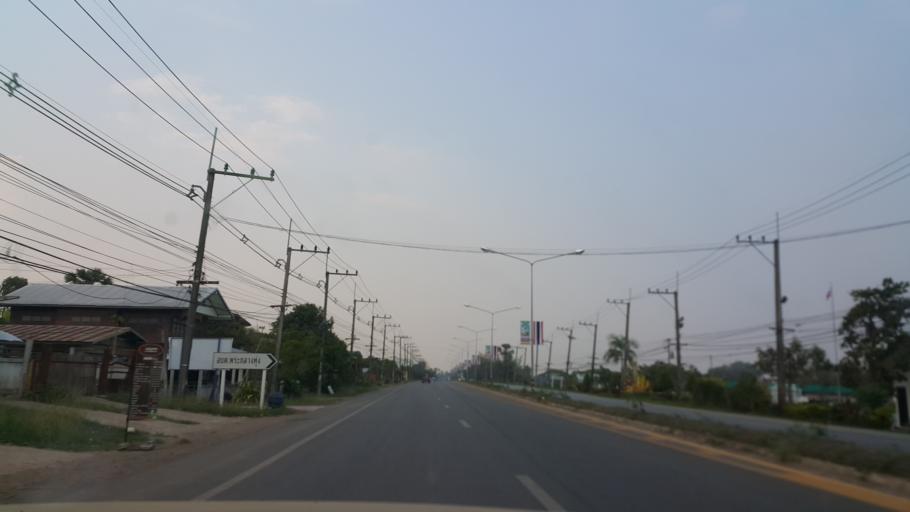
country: TH
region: Nakhon Phanom
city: That Phanom
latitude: 16.9955
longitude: 104.7236
